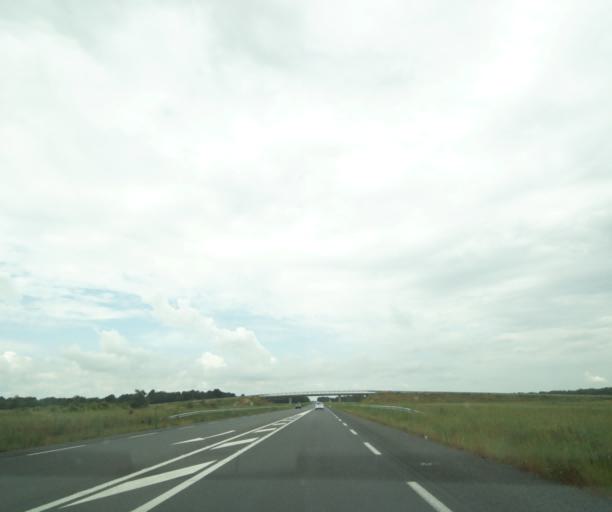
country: FR
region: Poitou-Charentes
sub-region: Departement des Deux-Sevres
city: Sainte-Verge
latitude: 47.0270
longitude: -0.2022
